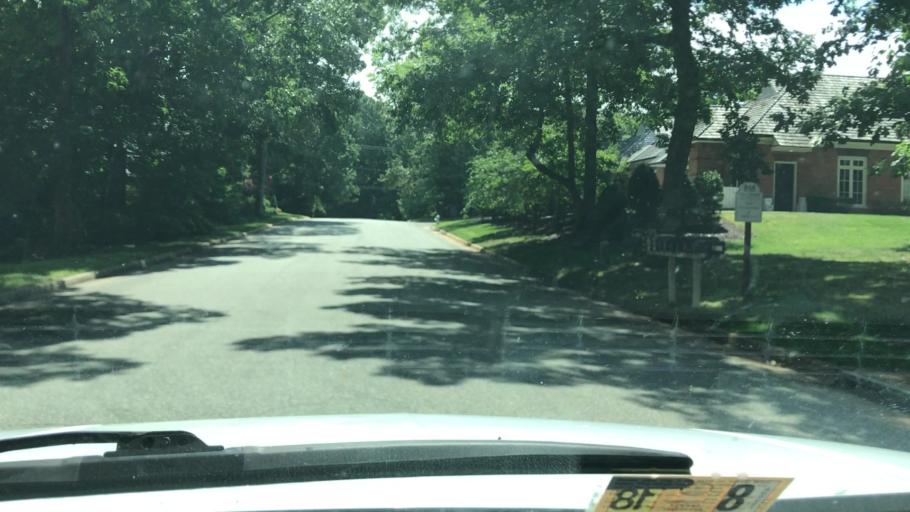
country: US
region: Virginia
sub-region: Chesterfield County
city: Brandermill
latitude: 37.5260
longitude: -77.6641
